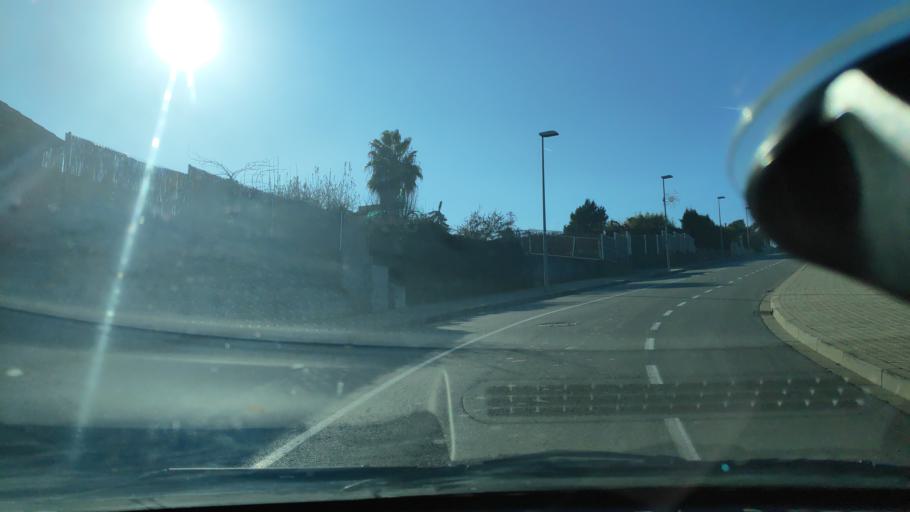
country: ES
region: Catalonia
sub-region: Provincia de Barcelona
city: Sant Quirze del Valles
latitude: 41.5213
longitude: 2.0881
